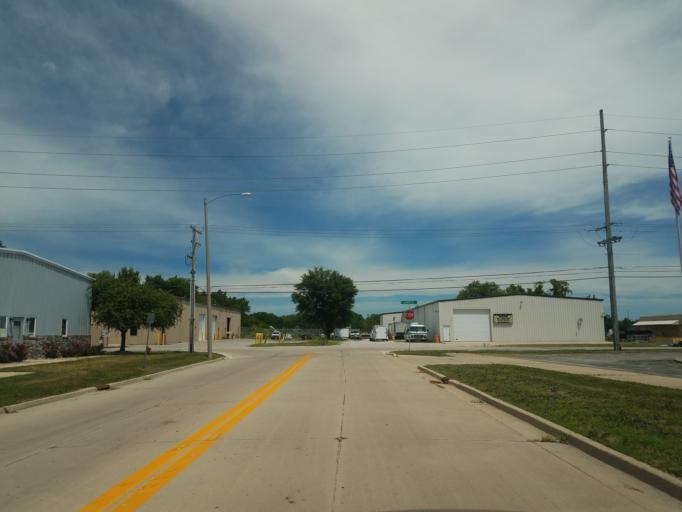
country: US
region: Illinois
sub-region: McLean County
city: Bloomington
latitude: 40.4629
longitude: -88.9883
